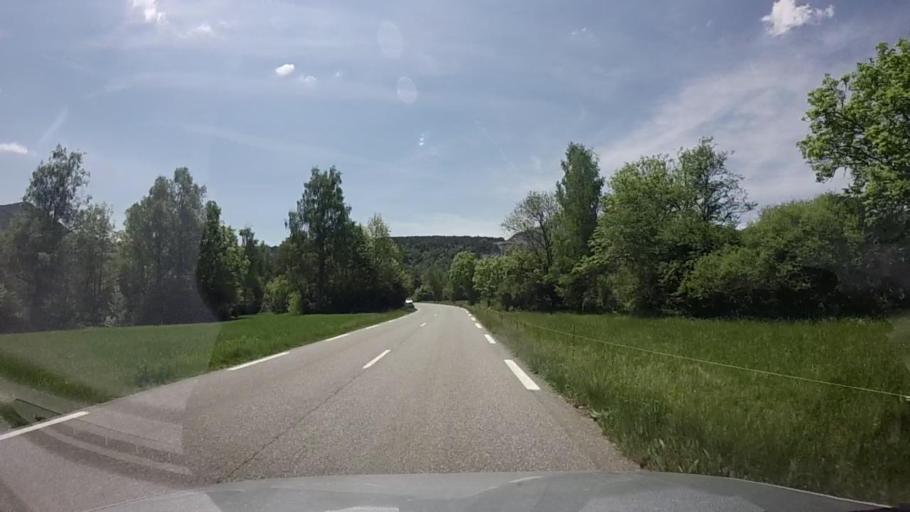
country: FR
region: Provence-Alpes-Cote d'Azur
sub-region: Departement des Alpes-de-Haute-Provence
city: Seyne-les-Alpes
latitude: 44.3815
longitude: 6.3268
